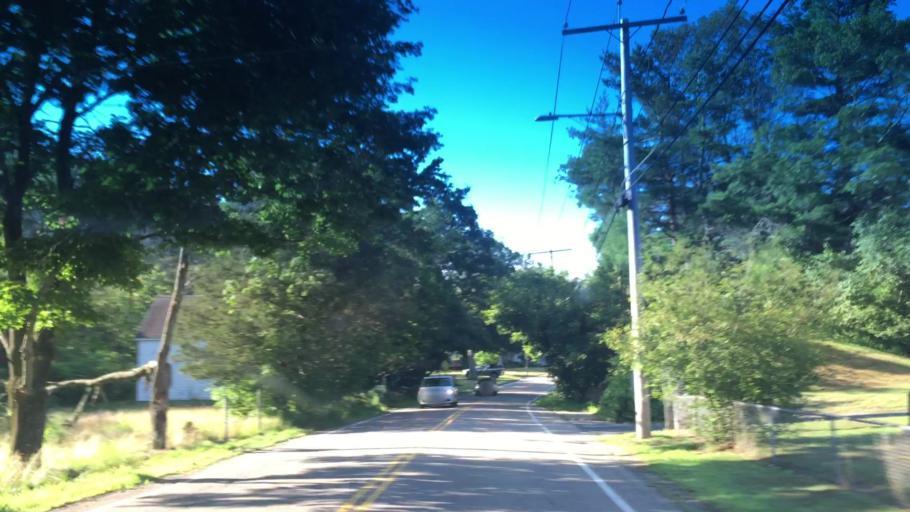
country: US
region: Massachusetts
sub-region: Norfolk County
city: Medway
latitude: 42.1490
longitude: -71.3916
